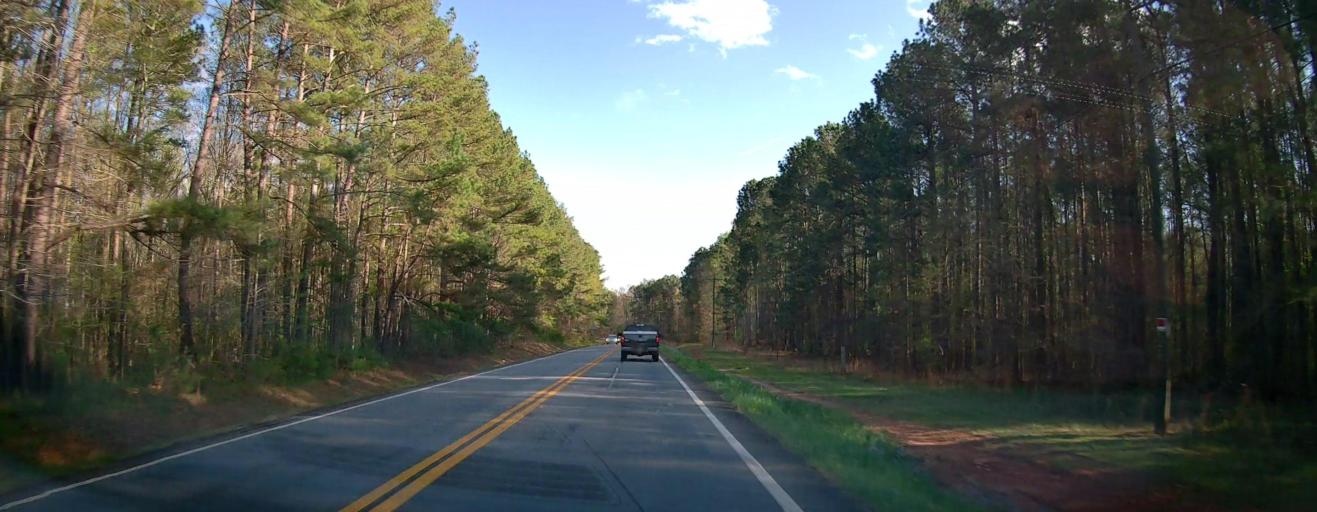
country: US
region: Georgia
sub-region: Putnam County
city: Eatonton
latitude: 33.1867
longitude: -83.4149
